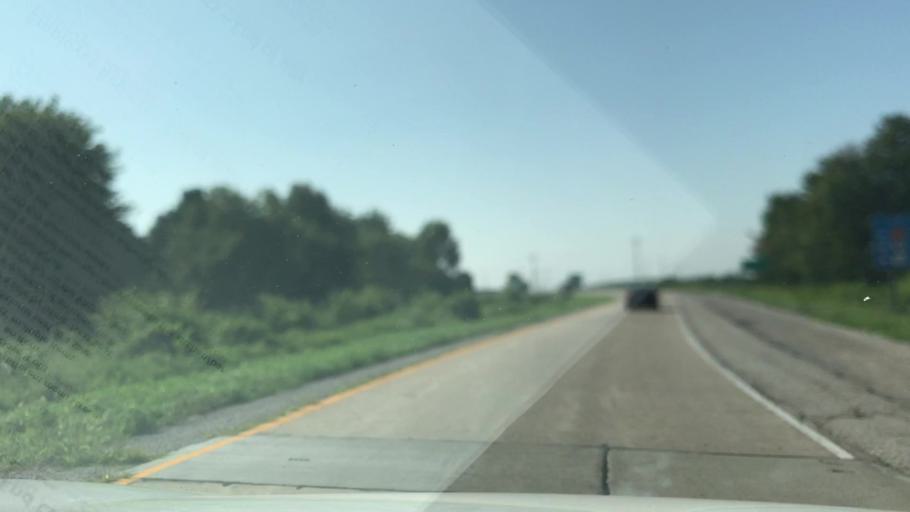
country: US
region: Illinois
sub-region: Saint Clair County
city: Scott Air Force Base
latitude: 38.5512
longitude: -89.8094
